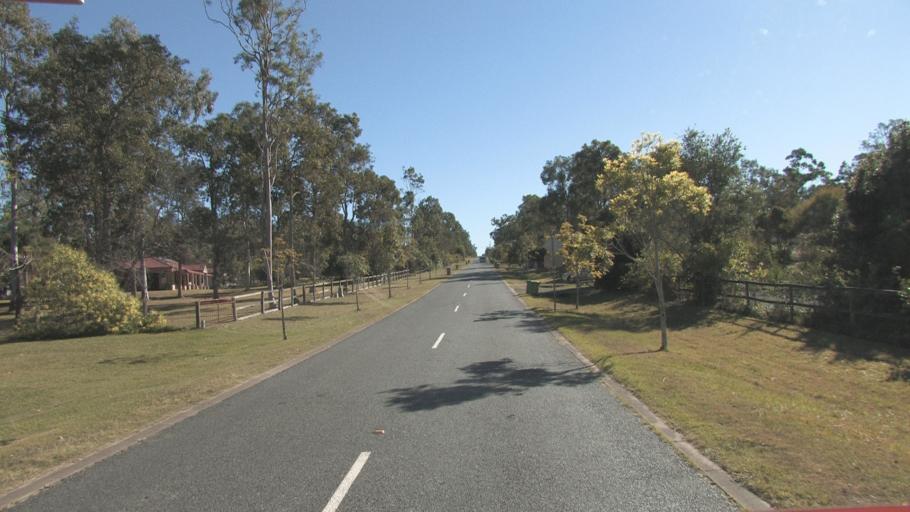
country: AU
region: Queensland
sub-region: Logan
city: North Maclean
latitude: -27.7511
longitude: 152.9569
